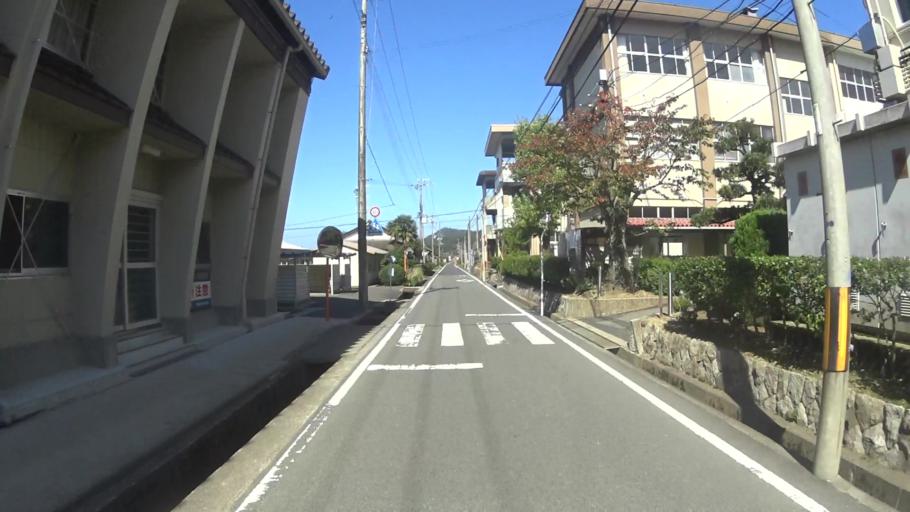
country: JP
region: Hyogo
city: Toyooka
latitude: 35.5919
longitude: 134.9316
